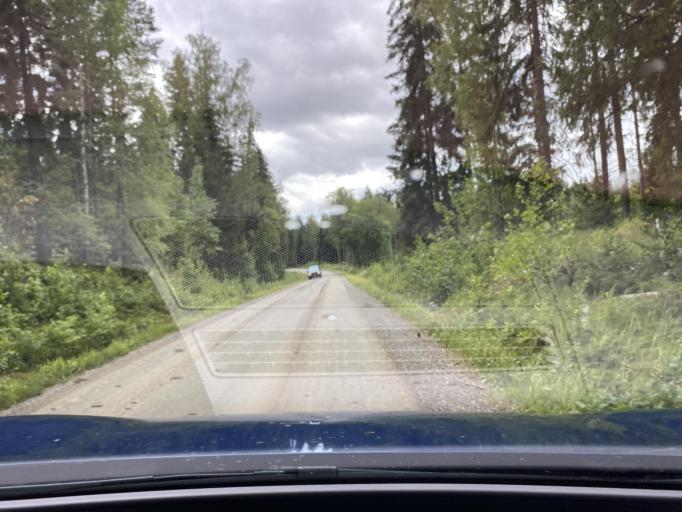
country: FI
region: Pirkanmaa
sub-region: Lounais-Pirkanmaa
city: Punkalaidun
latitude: 61.1948
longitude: 23.1814
